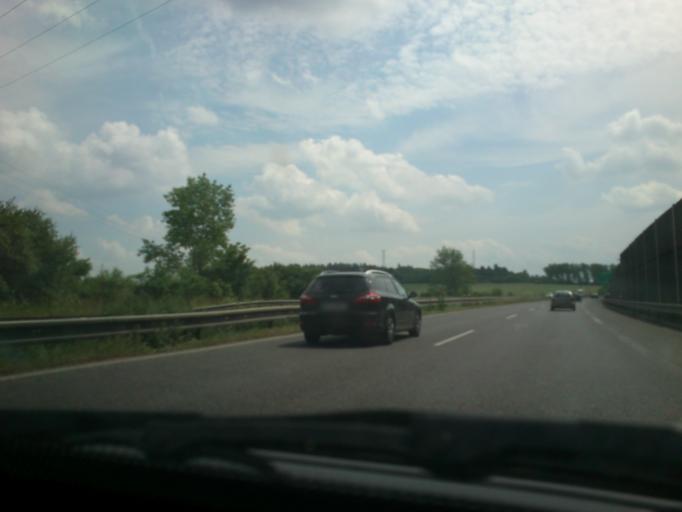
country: CZ
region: Central Bohemia
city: Lustenice
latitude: 50.3310
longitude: 14.8761
